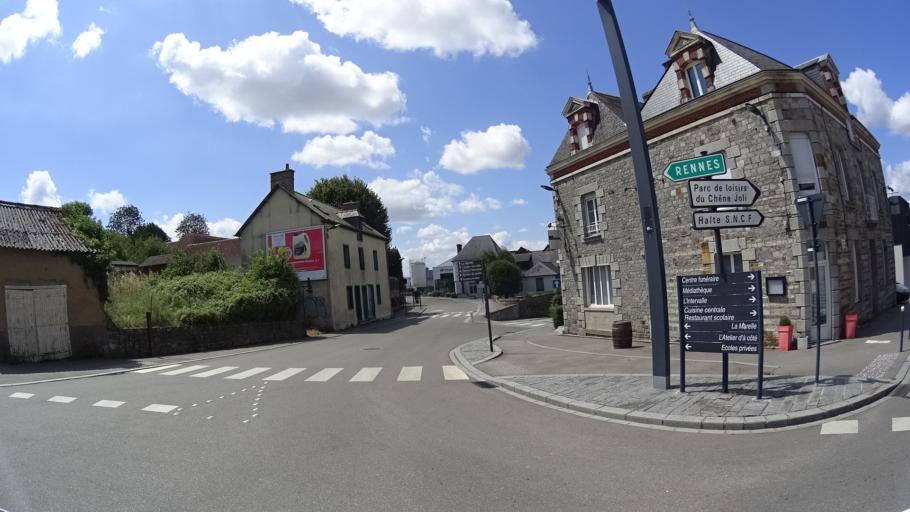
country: FR
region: Brittany
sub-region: Departement d'Ille-et-Vilaine
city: Noyal-sur-Vilaine
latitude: 48.1144
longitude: -1.5248
